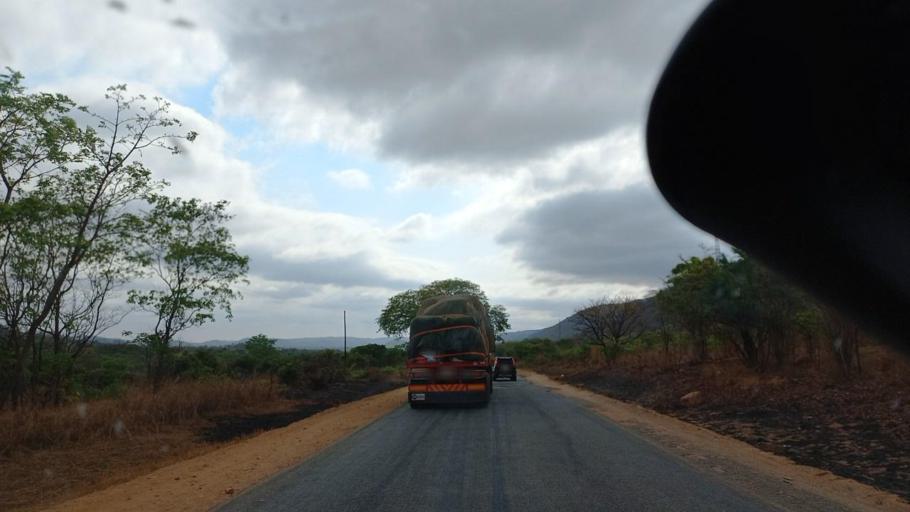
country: ZM
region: Lusaka
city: Chongwe
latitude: -15.1490
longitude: 29.3676
